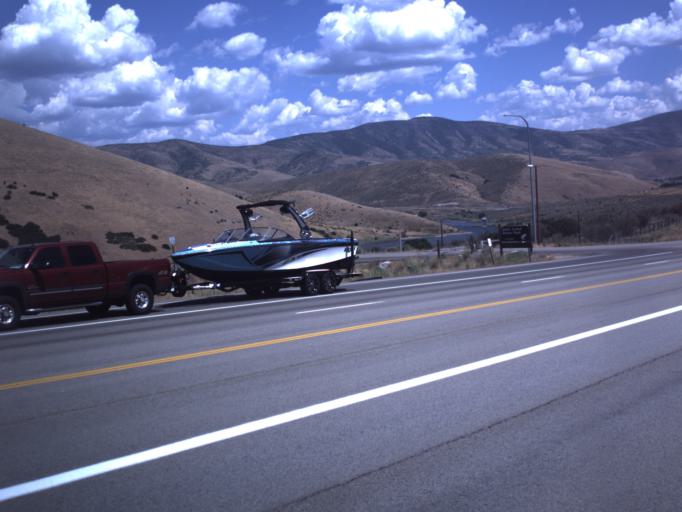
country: US
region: Utah
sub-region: Wasatch County
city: Midway
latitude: 40.4087
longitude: -111.5013
